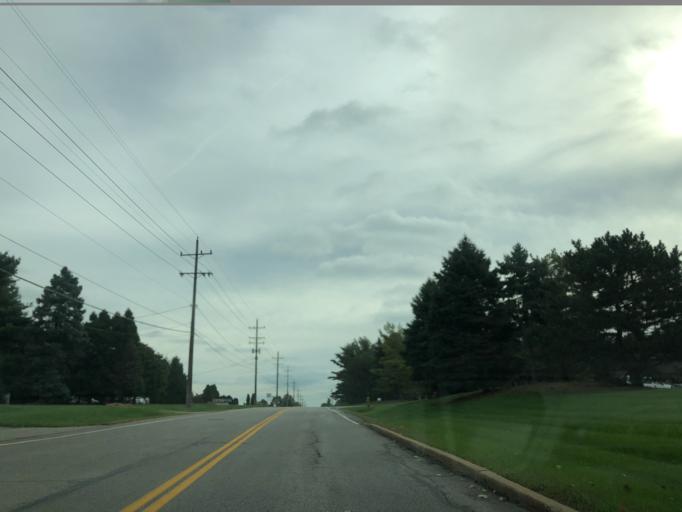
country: US
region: Ohio
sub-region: Cuyahoga County
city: Brecksville
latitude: 41.2831
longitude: -81.6266
